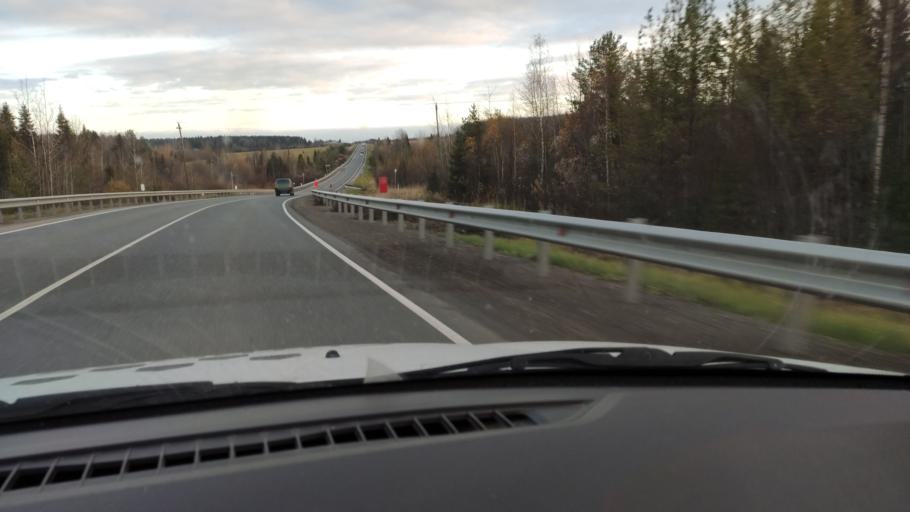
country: RU
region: Kirov
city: Omutninsk
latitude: 58.6944
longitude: 52.1277
